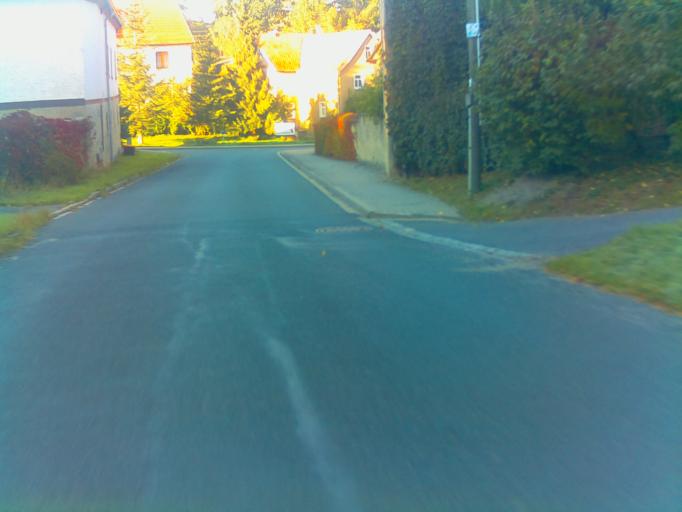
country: DE
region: Thuringia
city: Tautendorf
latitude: 50.8240
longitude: 11.8934
